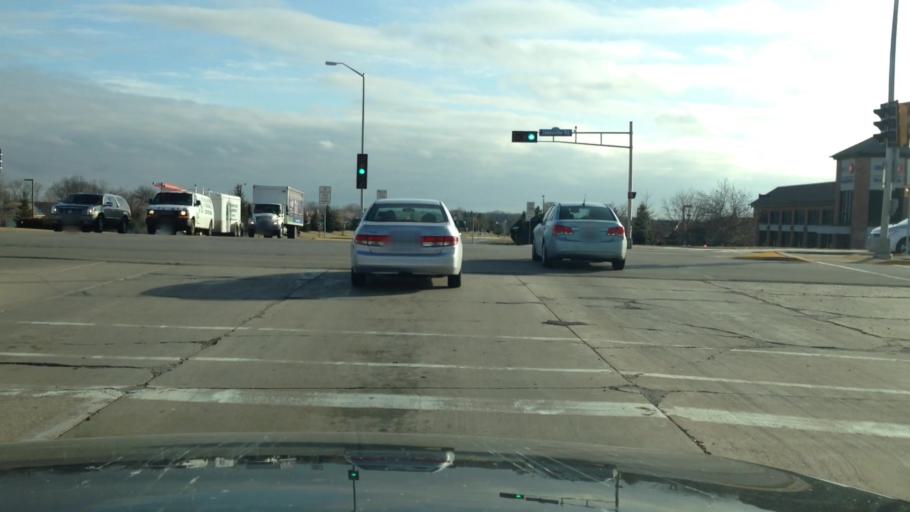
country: US
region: Wisconsin
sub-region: Waukesha County
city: Muskego
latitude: 42.9192
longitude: -88.1088
